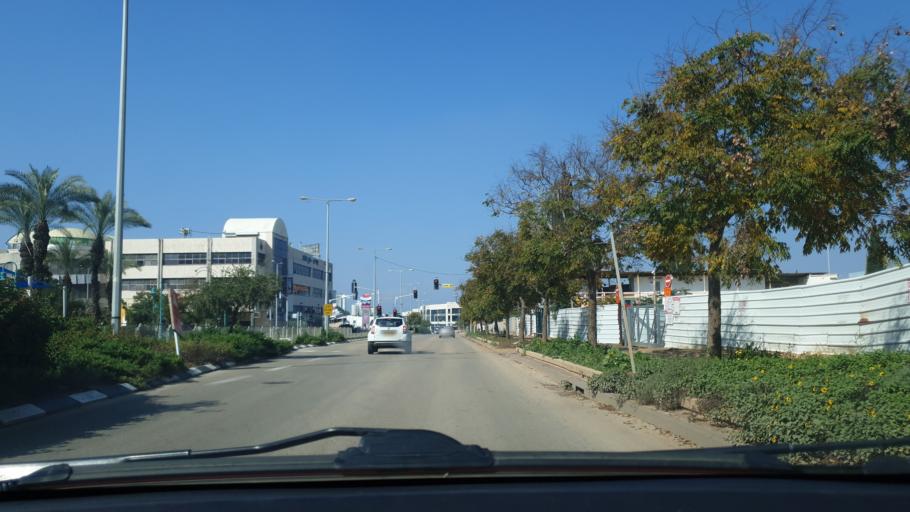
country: IL
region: Central District
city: Bet Dagan
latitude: 31.9749
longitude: 34.8147
